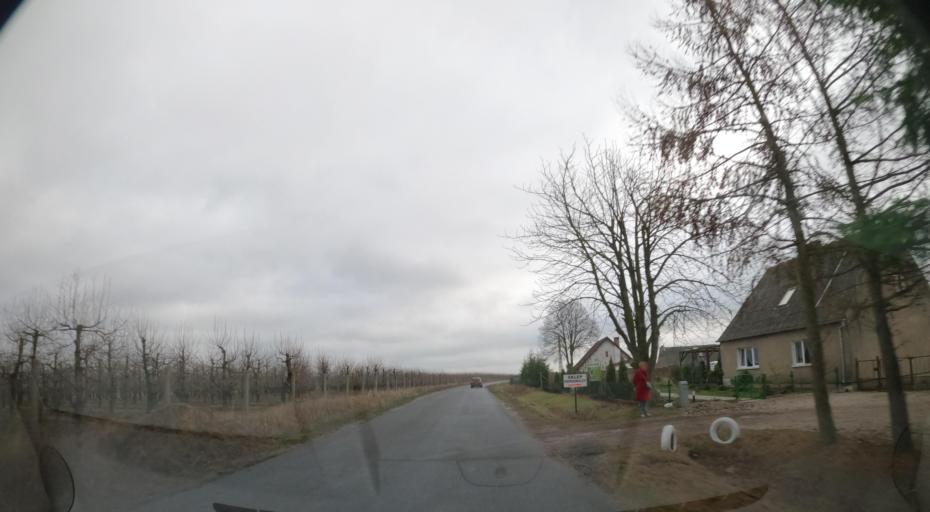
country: PL
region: Greater Poland Voivodeship
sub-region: Powiat pilski
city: Lobzenica
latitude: 53.2449
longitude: 17.2936
